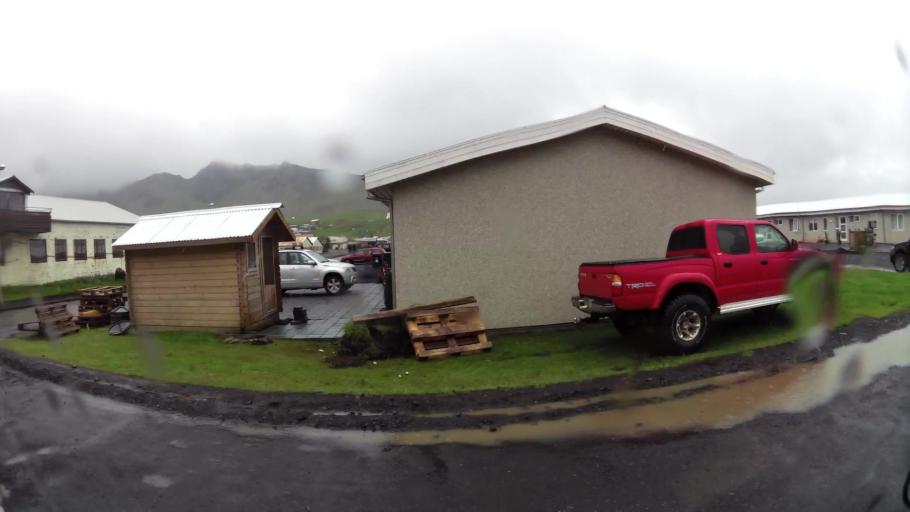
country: IS
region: South
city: Vestmannaeyjar
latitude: 63.4165
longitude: -19.0131
